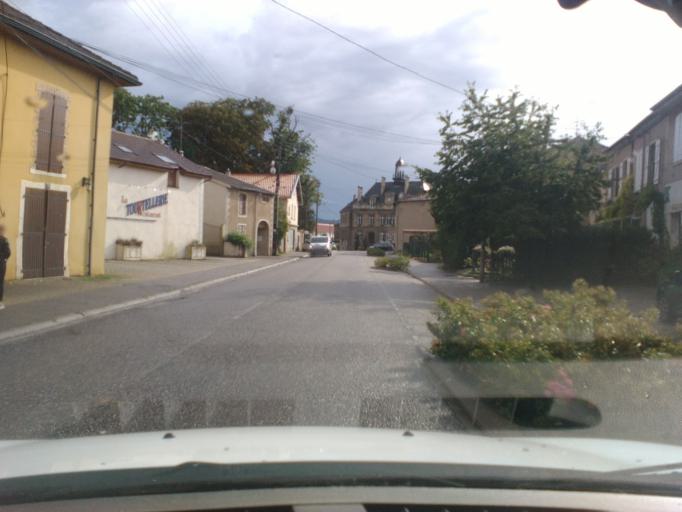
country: FR
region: Lorraine
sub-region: Departement de Meurthe-et-Moselle
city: Vezelise
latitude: 48.4706
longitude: 6.1408
